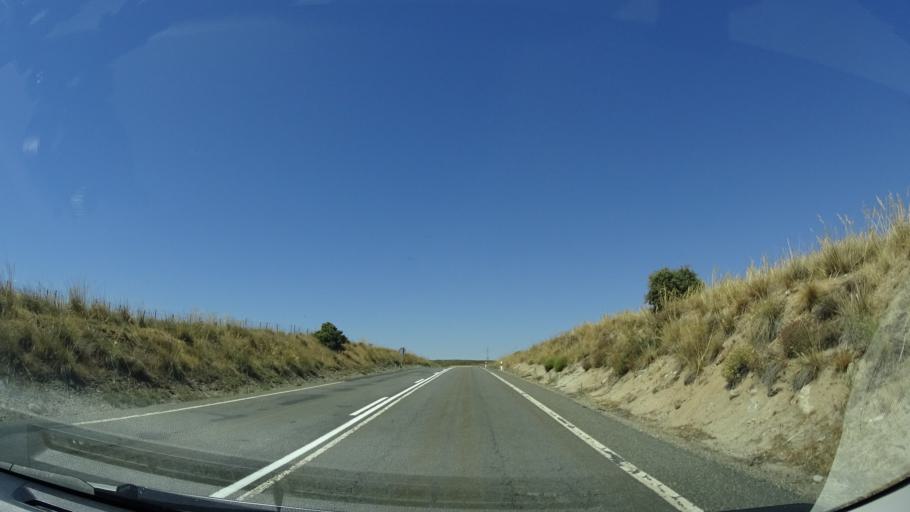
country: ES
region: Castille and Leon
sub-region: Provincia de Avila
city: Tornadizos de Avila
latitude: 40.6097
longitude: -4.5619
